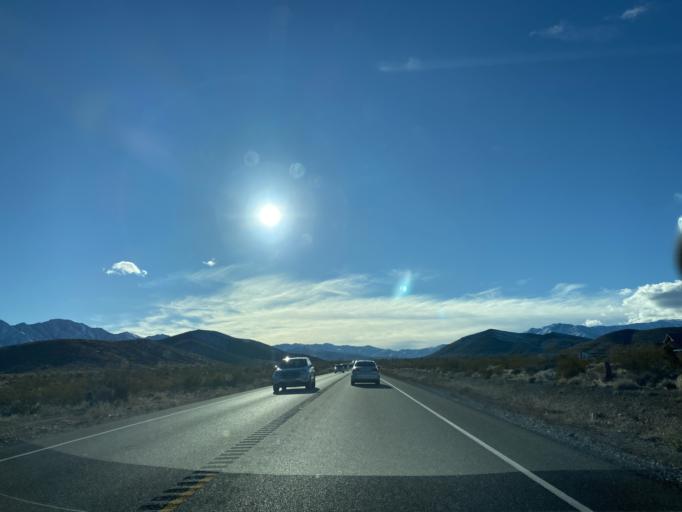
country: US
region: Nevada
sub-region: Clark County
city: Summerlin South
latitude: 36.2954
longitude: -115.4208
